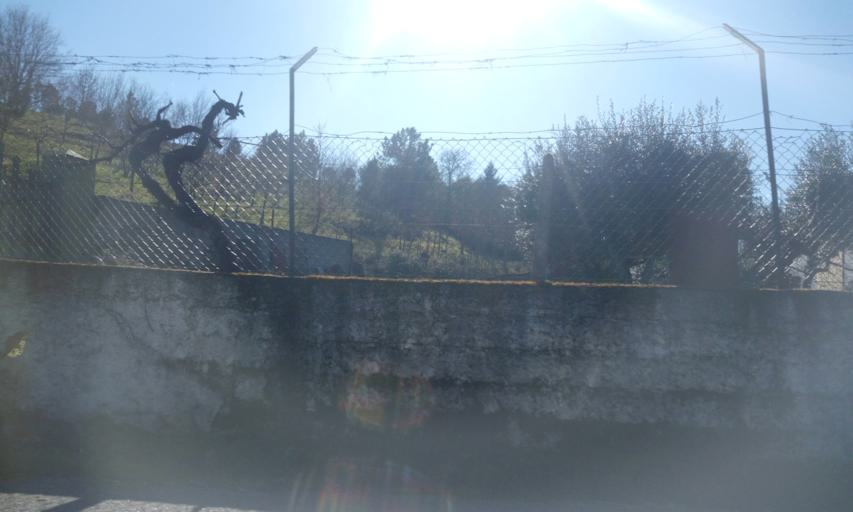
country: PT
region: Guarda
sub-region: Seia
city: Seia
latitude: 40.4741
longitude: -7.6229
